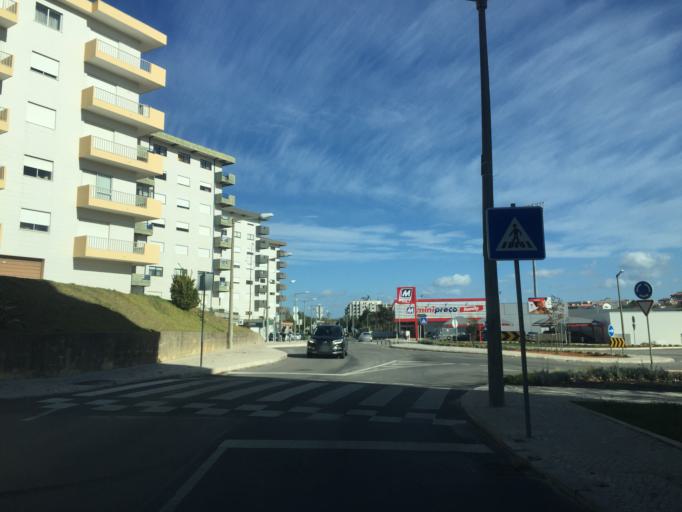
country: PT
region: Coimbra
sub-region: Figueira da Foz
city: Figueira da Foz
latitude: 40.1636
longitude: -8.8615
